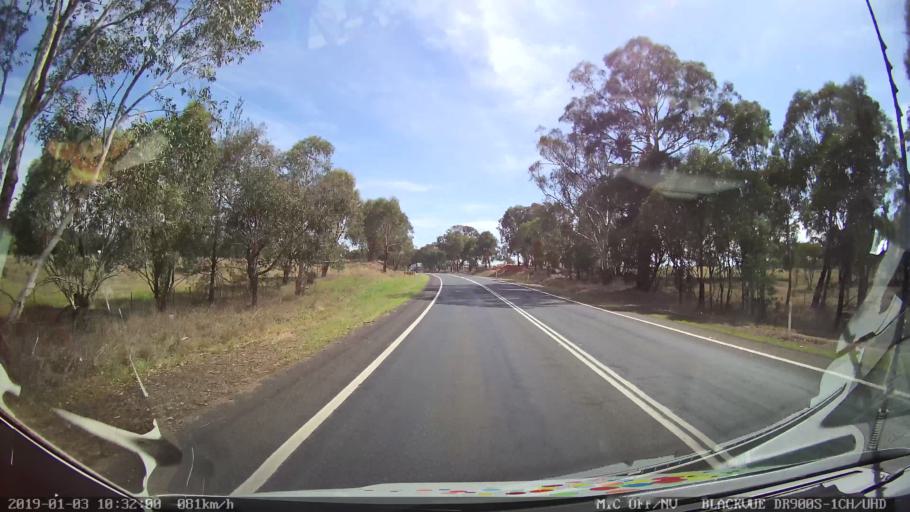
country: AU
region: New South Wales
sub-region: Young
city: Young
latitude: -34.3438
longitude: 148.2822
